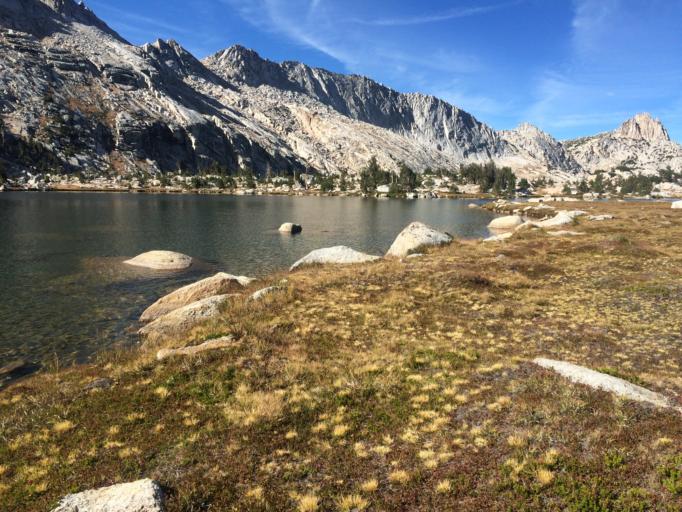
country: US
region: California
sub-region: Mariposa County
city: Yosemite Valley
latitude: 37.9367
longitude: -119.3335
